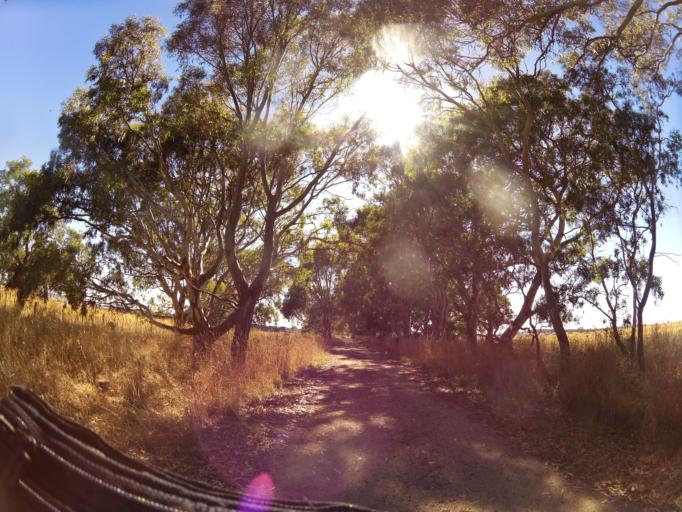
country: AU
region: Victoria
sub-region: Ballarat North
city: Delacombe
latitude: -37.6857
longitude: 143.4027
